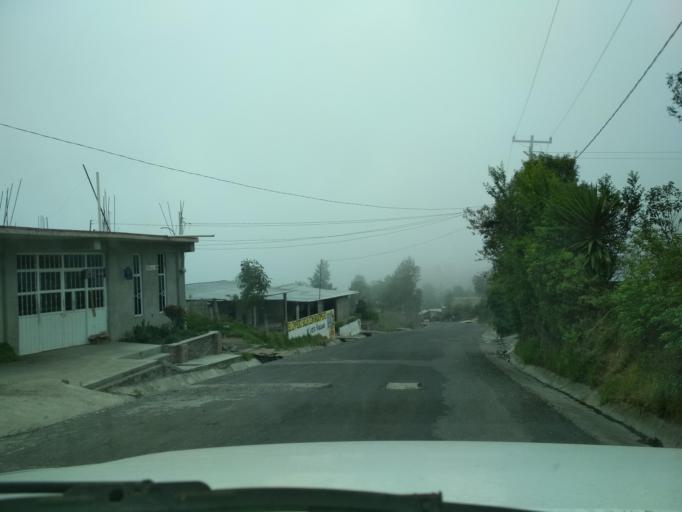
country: MX
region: Veracruz
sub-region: Mariano Escobedo
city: San Isidro el Berro
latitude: 18.9480
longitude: -97.2025
